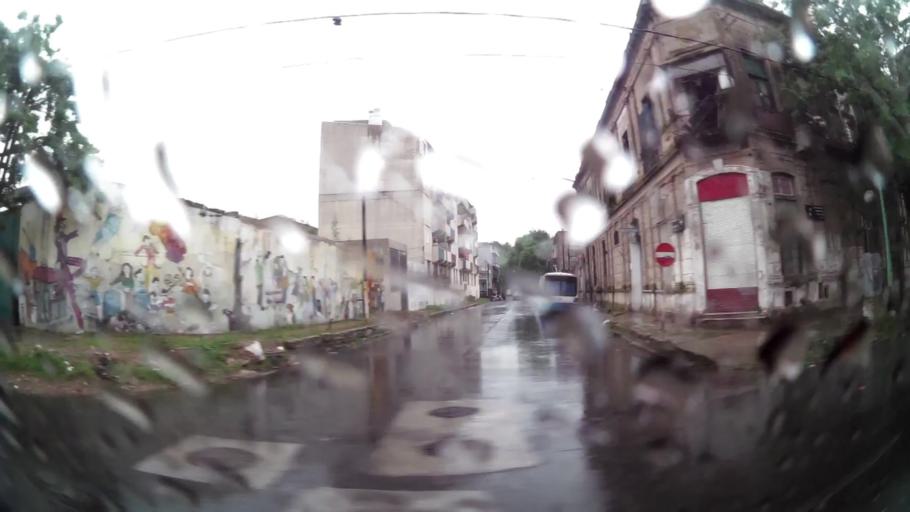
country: AR
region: Buenos Aires
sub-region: Partido de Avellaneda
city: Avellaneda
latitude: -34.6365
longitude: -58.3547
